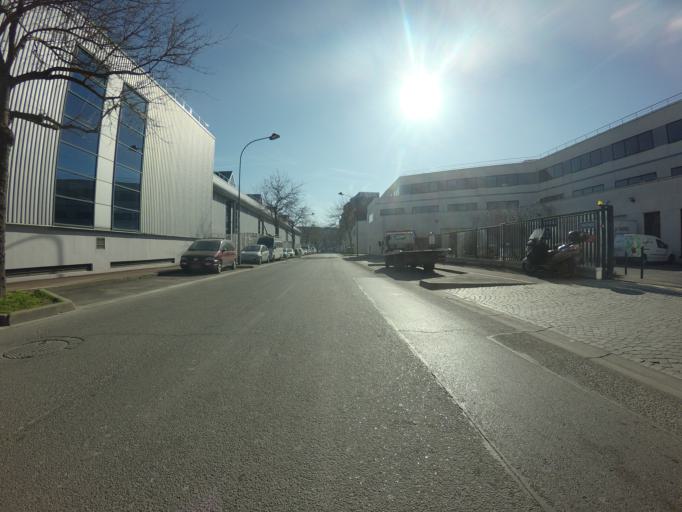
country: FR
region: Ile-de-France
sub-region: Departement des Hauts-de-Seine
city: Clichy
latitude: 48.9076
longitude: 2.3182
